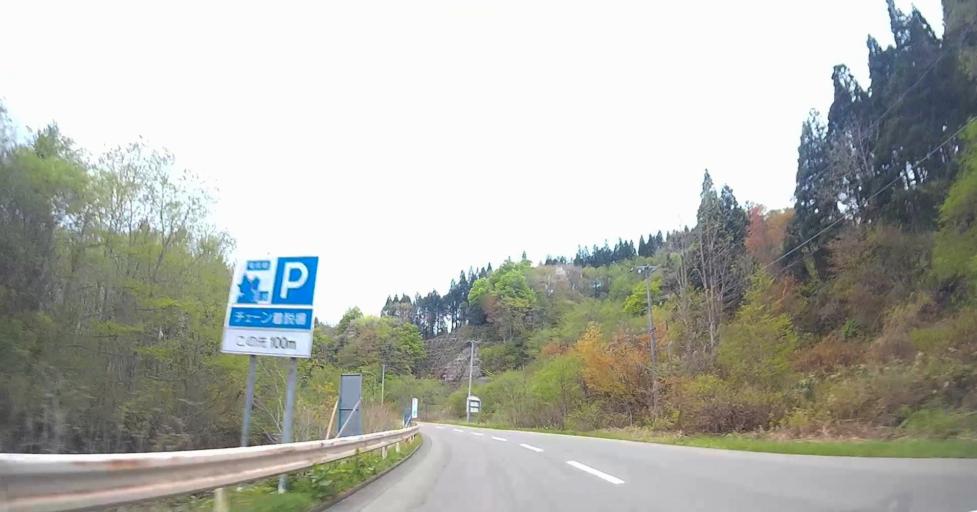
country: JP
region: Aomori
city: Goshogawara
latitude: 41.1188
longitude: 140.5237
